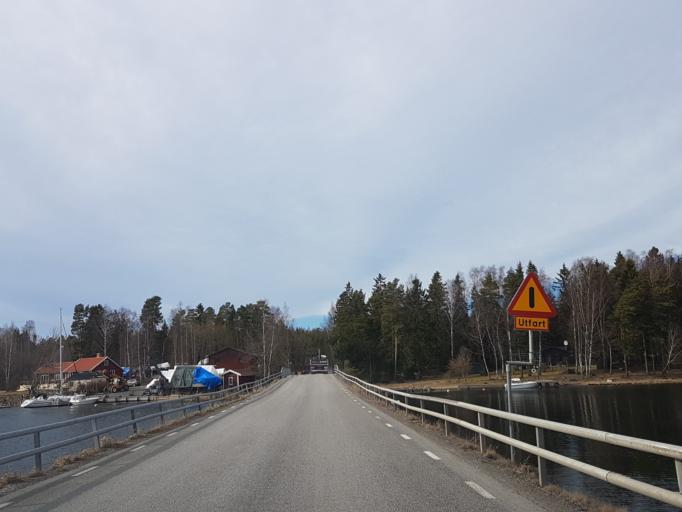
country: SE
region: Stockholm
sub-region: Norrtalje Kommun
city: Bjorko
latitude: 59.6629
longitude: 18.9018
